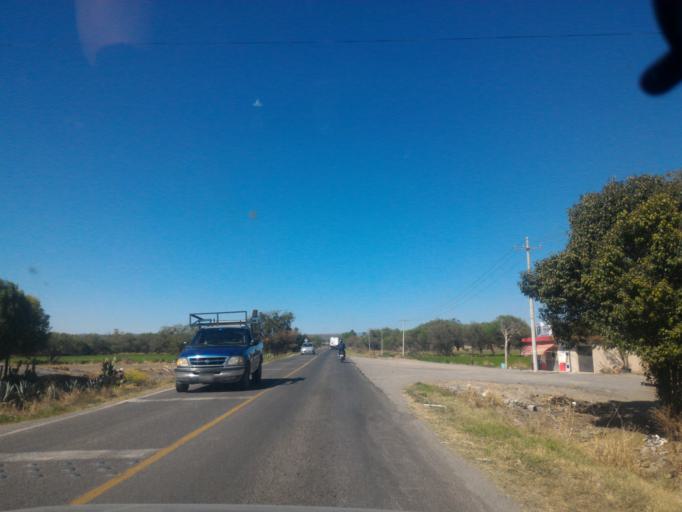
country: MX
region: Guanajuato
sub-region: San Francisco del Rincon
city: San Roque de Montes
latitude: 21.0037
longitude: -101.8049
